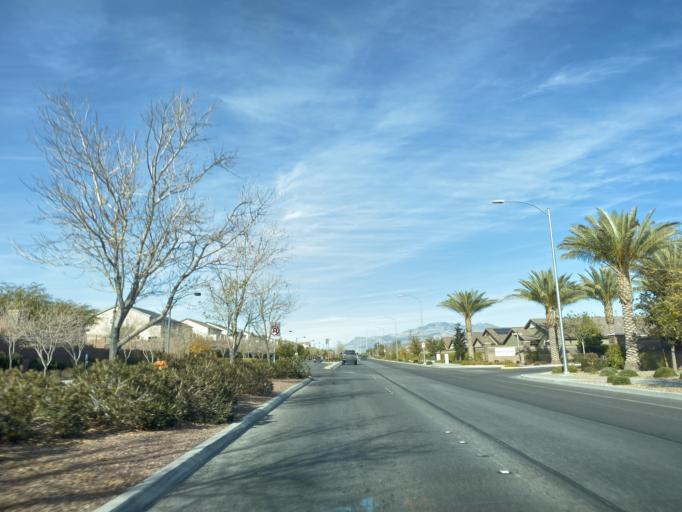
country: US
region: Nevada
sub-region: Clark County
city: Summerlin South
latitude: 36.2936
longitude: -115.3148
